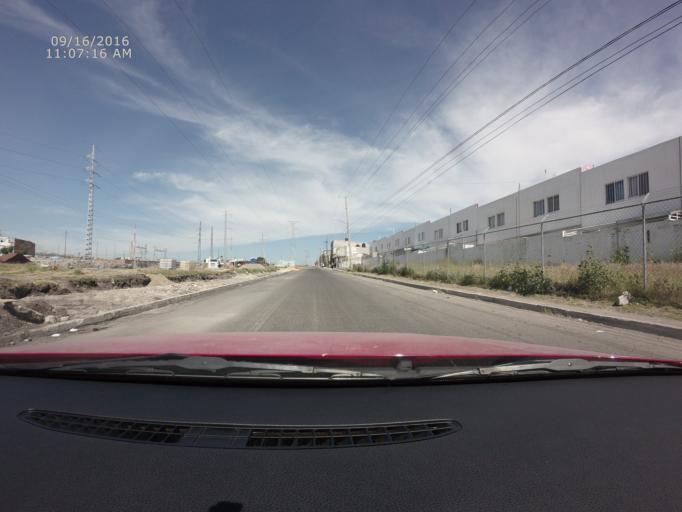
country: MX
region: Queretaro
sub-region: Queretaro
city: Sergio Villasenor
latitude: 20.6297
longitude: -100.4088
